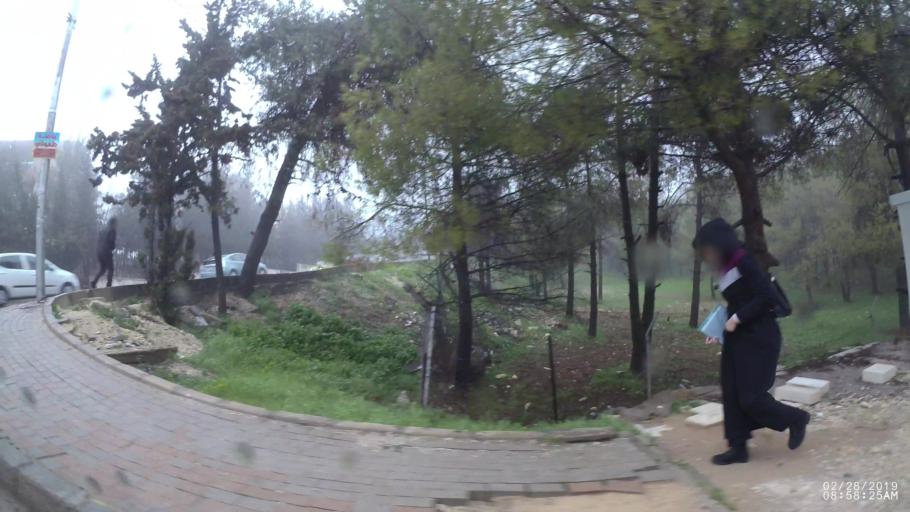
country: JO
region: Amman
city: Al Jubayhah
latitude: 32.0210
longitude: 35.8764
